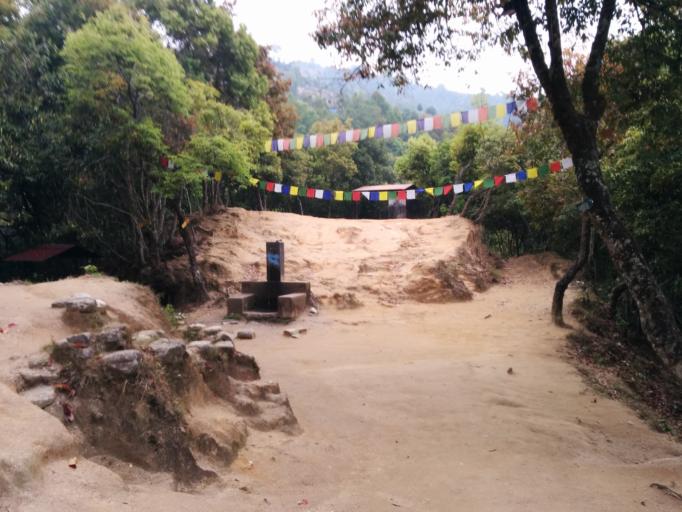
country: NP
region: Central Region
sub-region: Bagmati Zone
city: Bhaktapur
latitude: 27.7711
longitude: 85.4262
